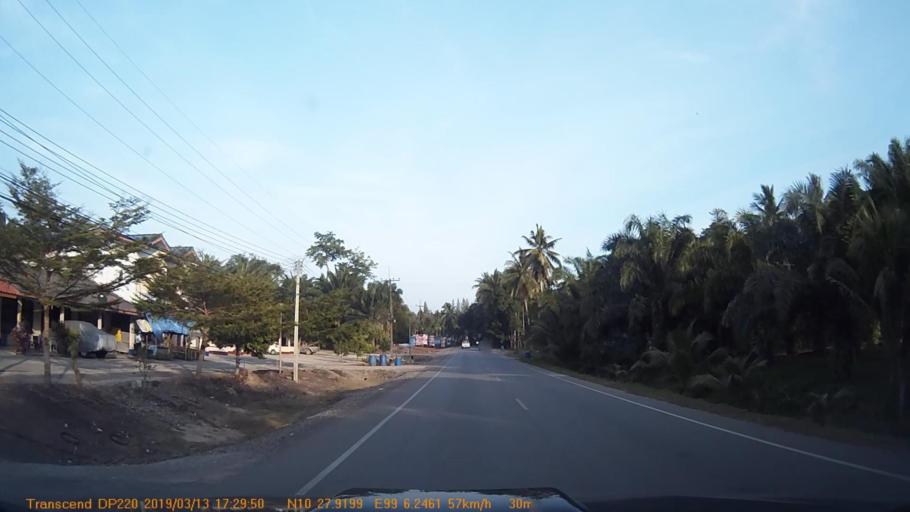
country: TH
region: Chumphon
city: Chumphon
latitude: 10.4653
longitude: 99.1042
